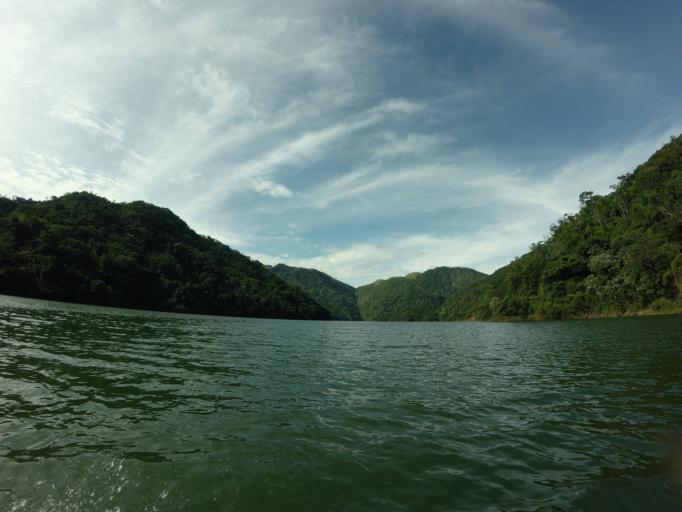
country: CO
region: Caldas
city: Norcasia
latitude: 5.5535
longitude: -74.9118
